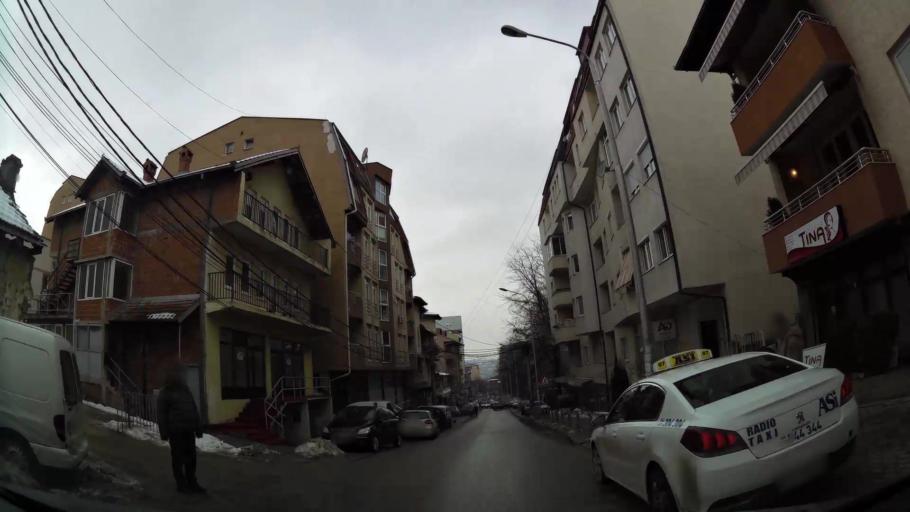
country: XK
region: Pristina
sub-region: Komuna e Prishtines
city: Pristina
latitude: 42.6601
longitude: 21.1697
